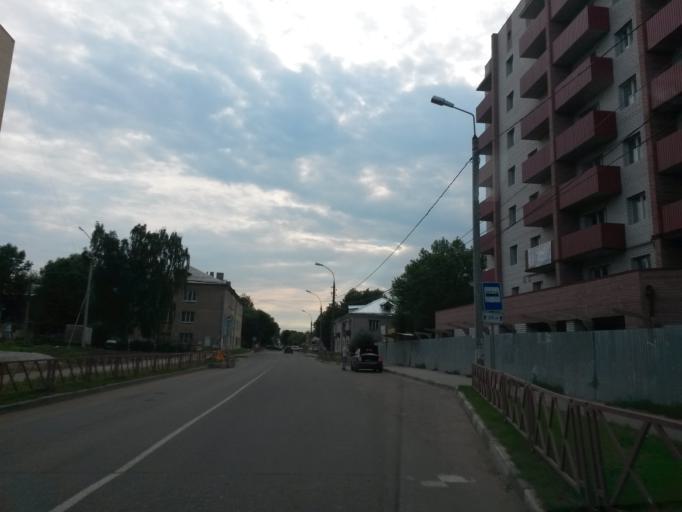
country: RU
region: Jaroslavl
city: Yaroslavl
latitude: 57.6060
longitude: 39.8182
